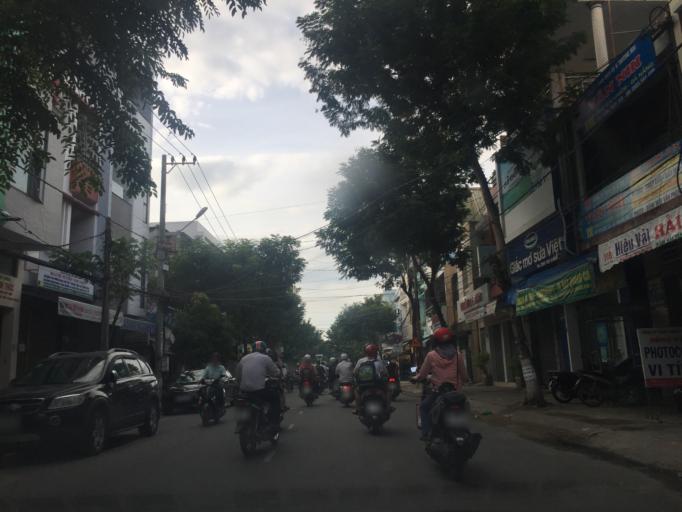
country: VN
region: Da Nang
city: Da Nang
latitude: 16.0760
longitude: 108.2123
